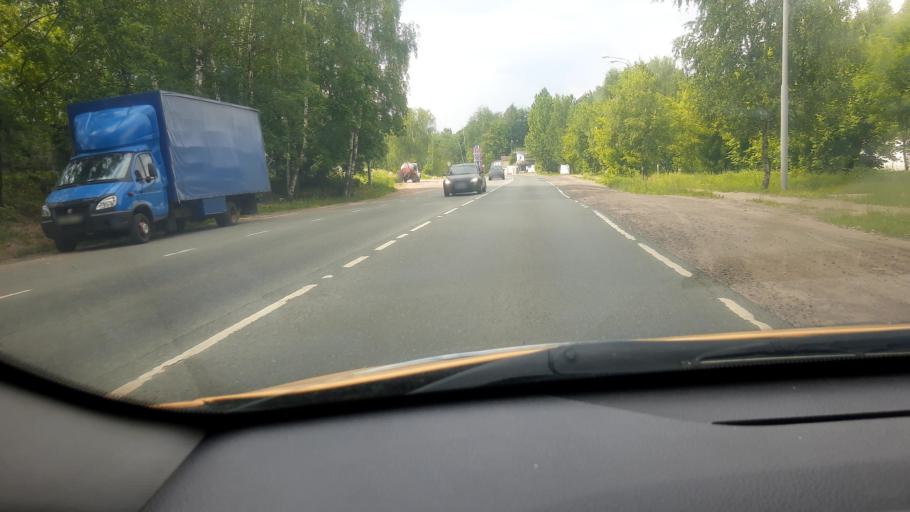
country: RU
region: Moskovskaya
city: Troitsk
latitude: 55.4941
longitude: 37.2970
